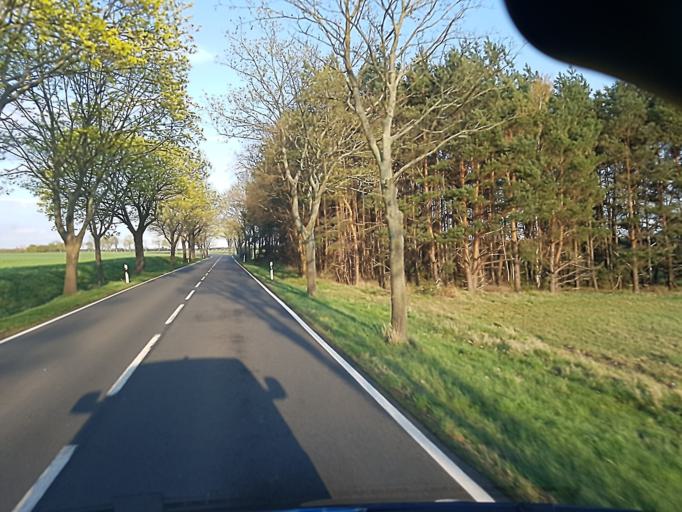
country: DE
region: Saxony
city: Bad Duben
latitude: 51.6222
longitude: 12.5357
